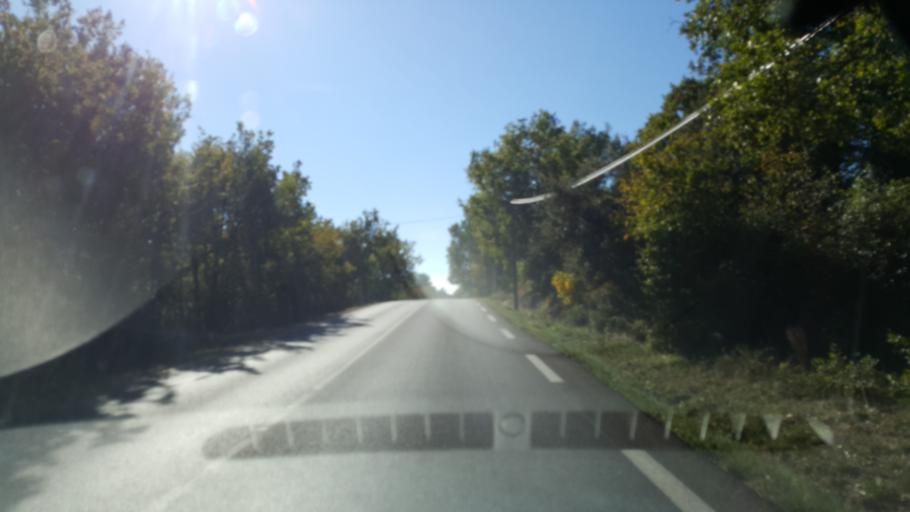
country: FR
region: Provence-Alpes-Cote d'Azur
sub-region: Departement du Var
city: Saint-Maximin-la-Sainte-Baume
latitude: 43.4304
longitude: 5.8494
